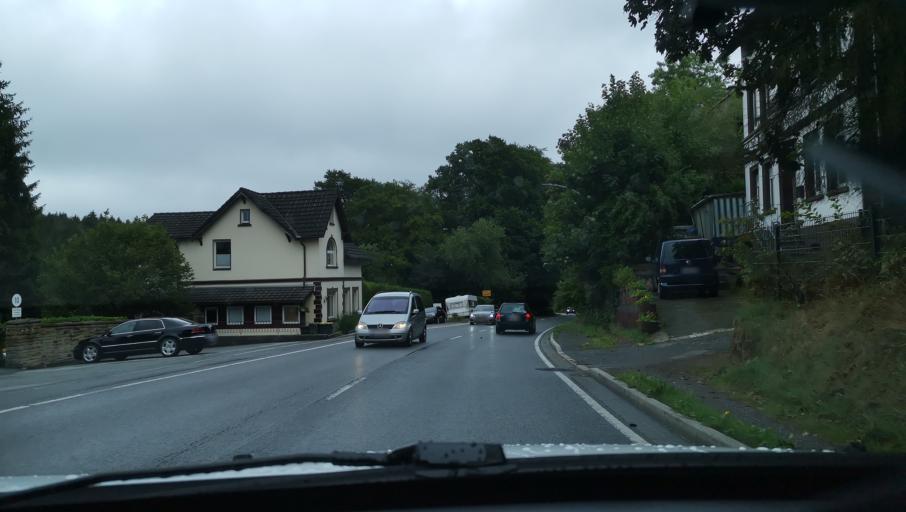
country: DE
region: North Rhine-Westphalia
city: Halver
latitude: 51.1955
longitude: 7.5112
